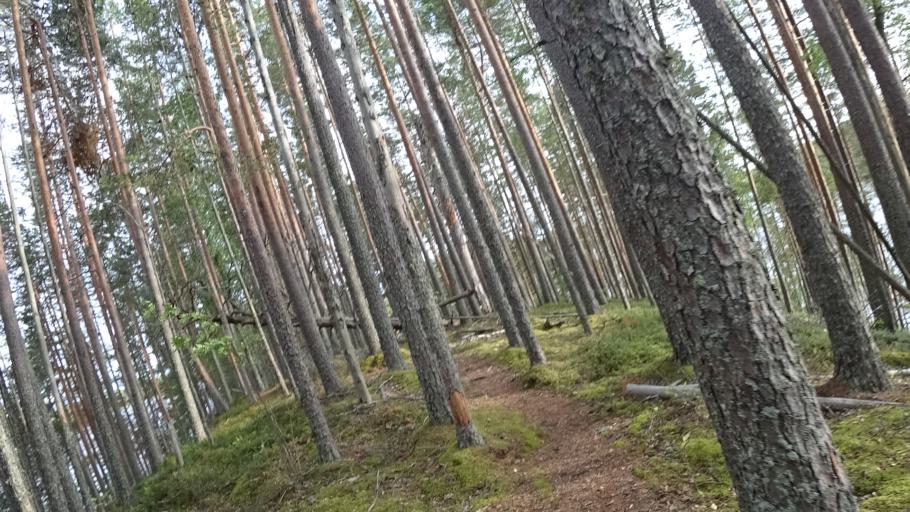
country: FI
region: North Karelia
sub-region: Joensuu
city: Ilomantsi
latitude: 62.5684
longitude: 31.1805
